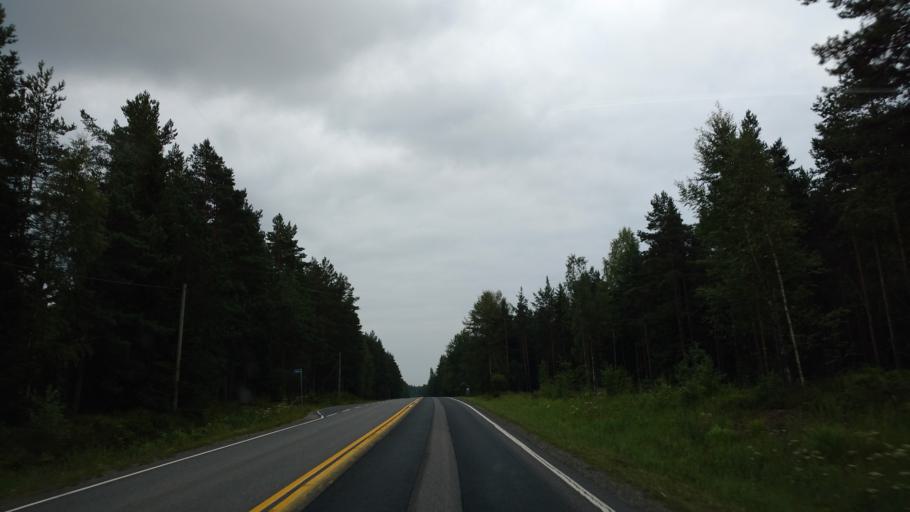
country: FI
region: Varsinais-Suomi
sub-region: Salo
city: Halikko
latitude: 60.4636
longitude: 23.0186
